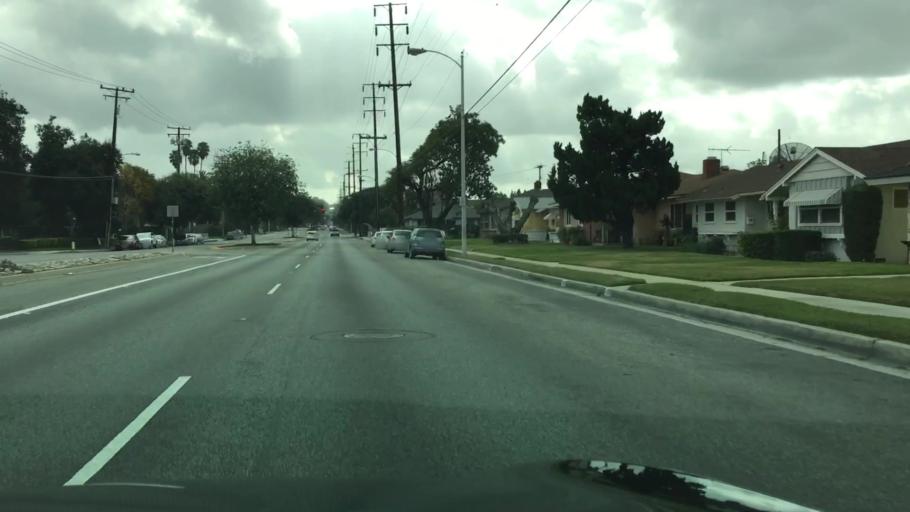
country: US
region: California
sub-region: Los Angeles County
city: Covina
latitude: 34.0668
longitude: -117.9079
